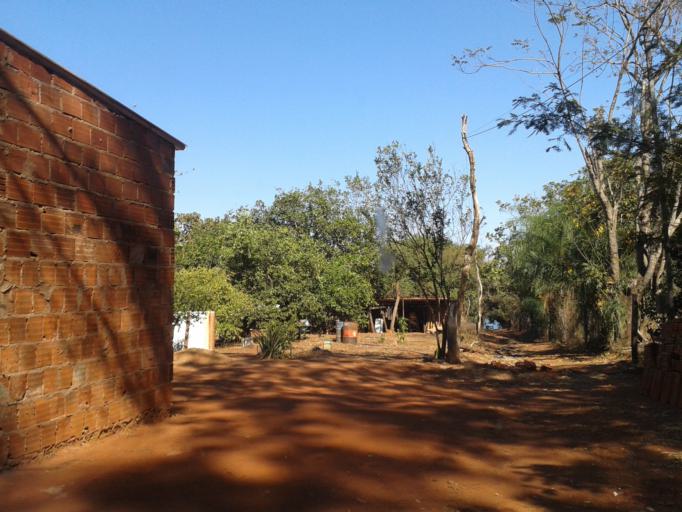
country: BR
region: Minas Gerais
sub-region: Santa Vitoria
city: Santa Vitoria
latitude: -19.0088
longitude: -50.3843
